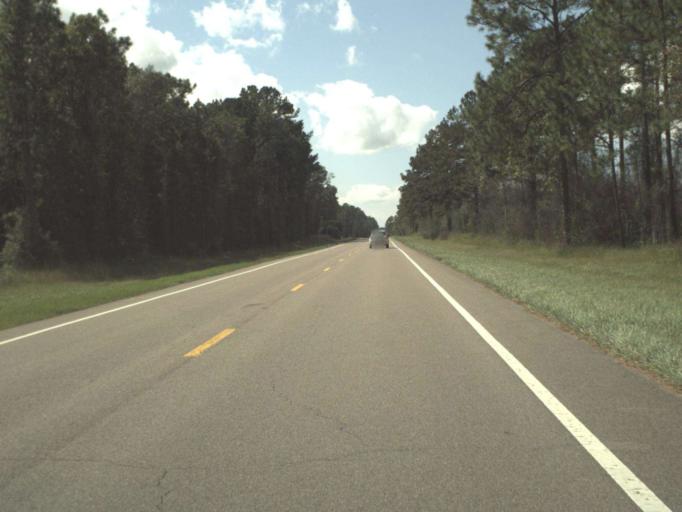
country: US
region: Florida
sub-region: Walton County
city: Freeport
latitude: 30.4909
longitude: -85.9403
